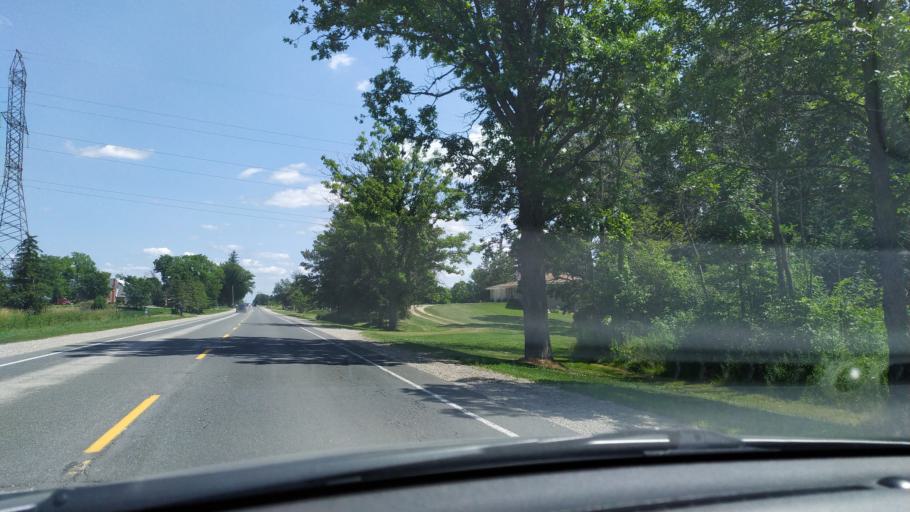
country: CA
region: Ontario
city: Stratford
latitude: 43.3523
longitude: -80.9443
